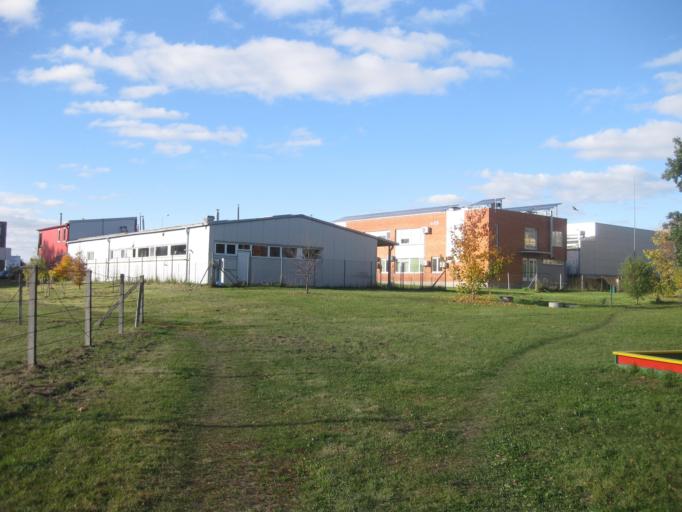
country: LT
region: Kauno apskritis
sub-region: Kauno rajonas
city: Garliava
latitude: 54.8308
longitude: 23.8770
